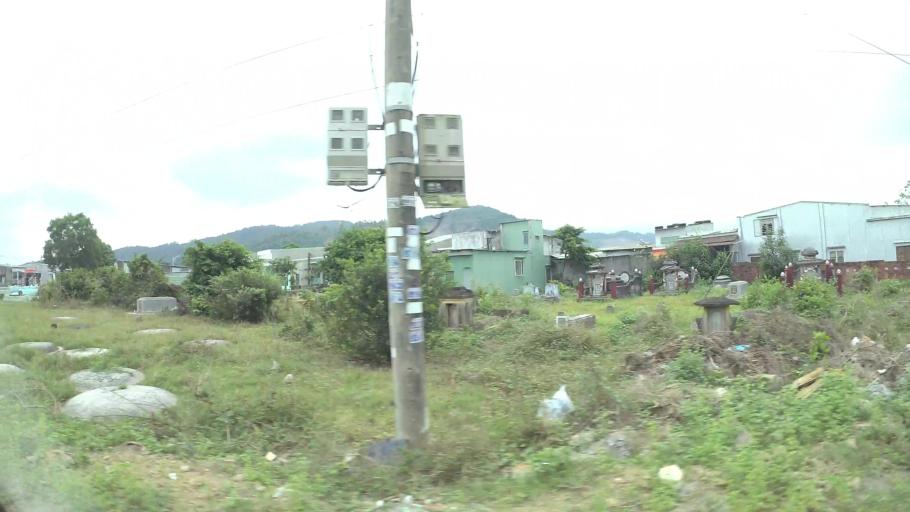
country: VN
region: Da Nang
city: Lien Chieu
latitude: 16.0474
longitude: 108.1702
